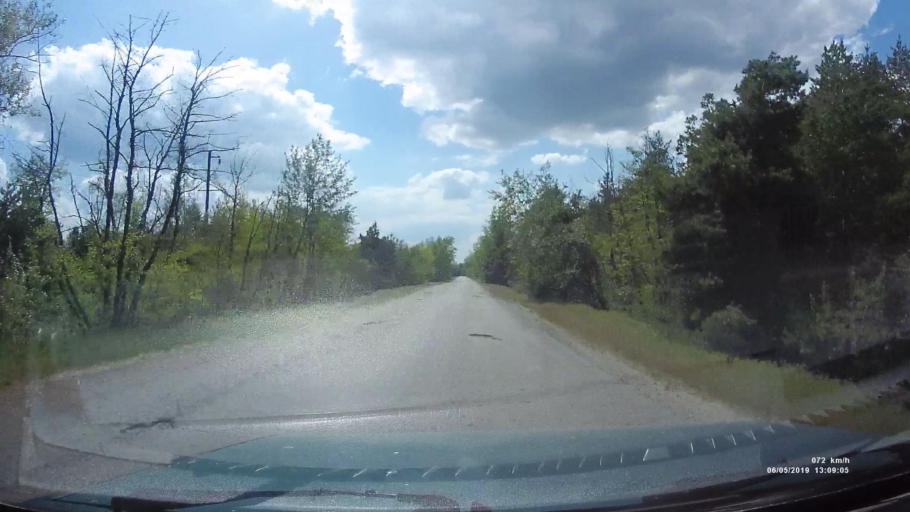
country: RU
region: Rostov
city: Ust'-Donetskiy
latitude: 47.7711
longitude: 40.9883
